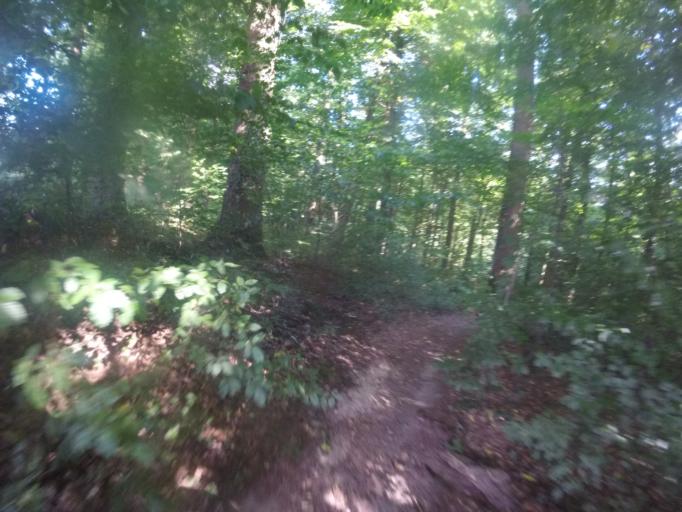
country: DE
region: Baden-Wuerttemberg
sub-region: Regierungsbezirk Stuttgart
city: Oberstenfeld
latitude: 49.0069
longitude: 9.3481
